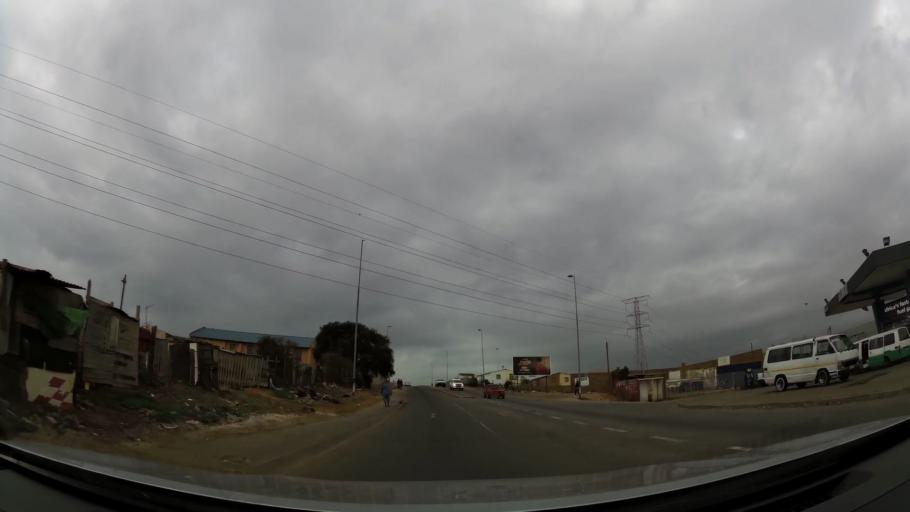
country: ZA
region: Eastern Cape
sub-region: Nelson Mandela Bay Metropolitan Municipality
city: Port Elizabeth
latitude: -33.8906
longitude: 25.5885
